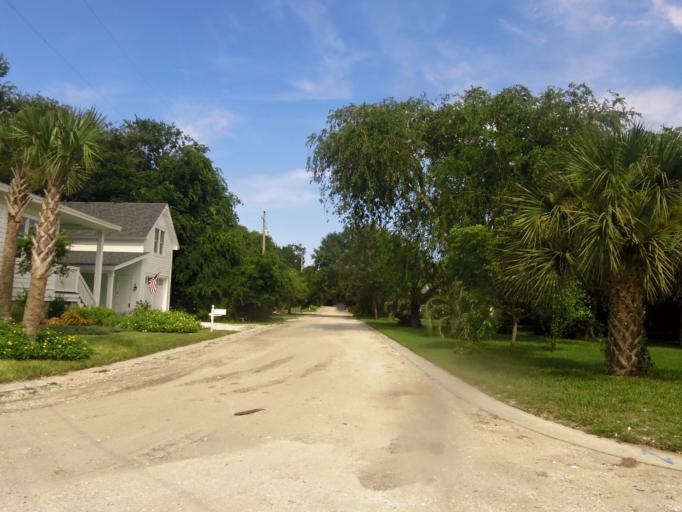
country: US
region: Florida
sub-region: Nassau County
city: Fernandina Beach
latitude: 30.6883
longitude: -81.4563
